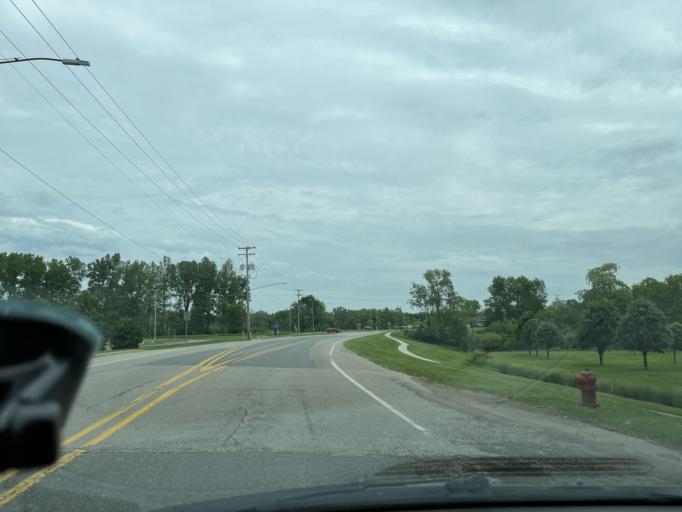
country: US
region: Michigan
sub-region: Barry County
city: Hastings
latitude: 42.6470
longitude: -85.3088
